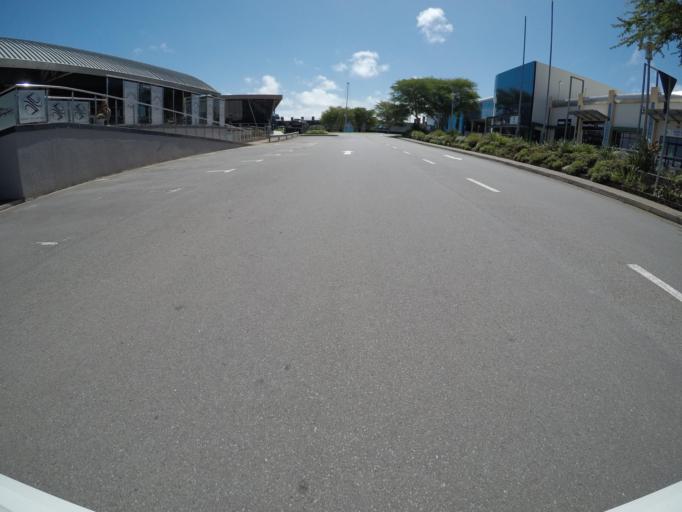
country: ZA
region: Eastern Cape
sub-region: Buffalo City Metropolitan Municipality
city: East London
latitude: -32.9519
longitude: 27.9295
